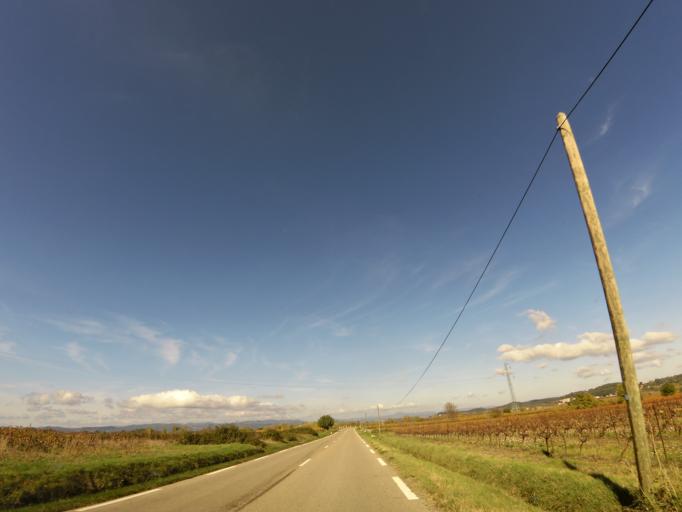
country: FR
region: Languedoc-Roussillon
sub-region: Departement du Gard
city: Ledignan
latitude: 44.0023
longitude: 4.1035
